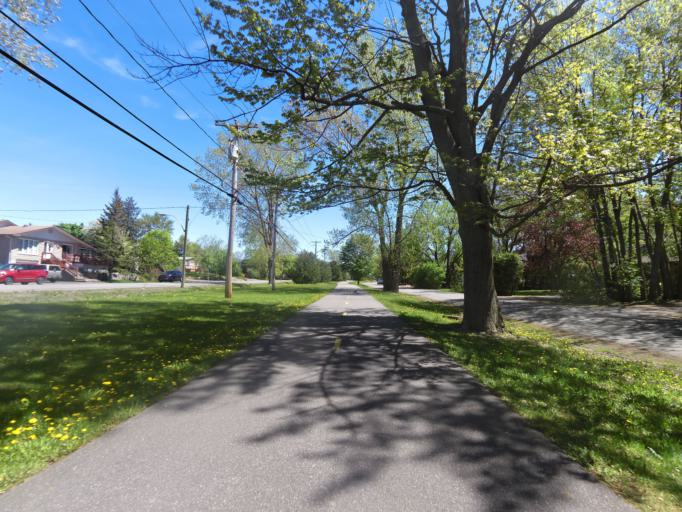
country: CA
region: Ontario
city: Bells Corners
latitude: 45.4038
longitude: -75.8705
